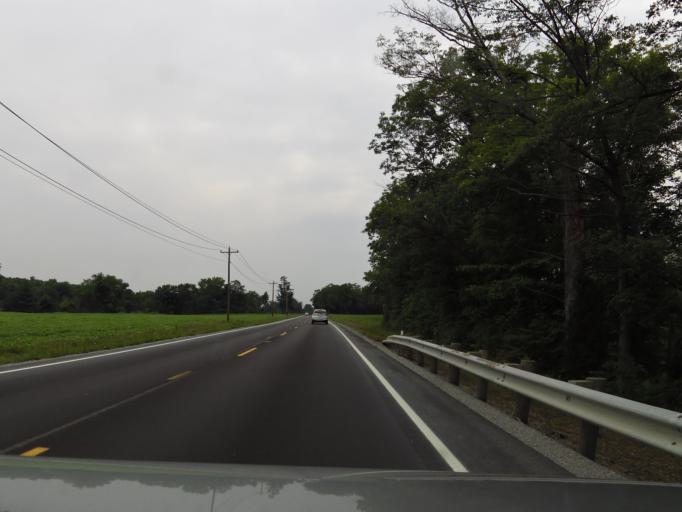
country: US
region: Ohio
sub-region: Clinton County
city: Blanchester
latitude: 39.2122
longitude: -83.9161
